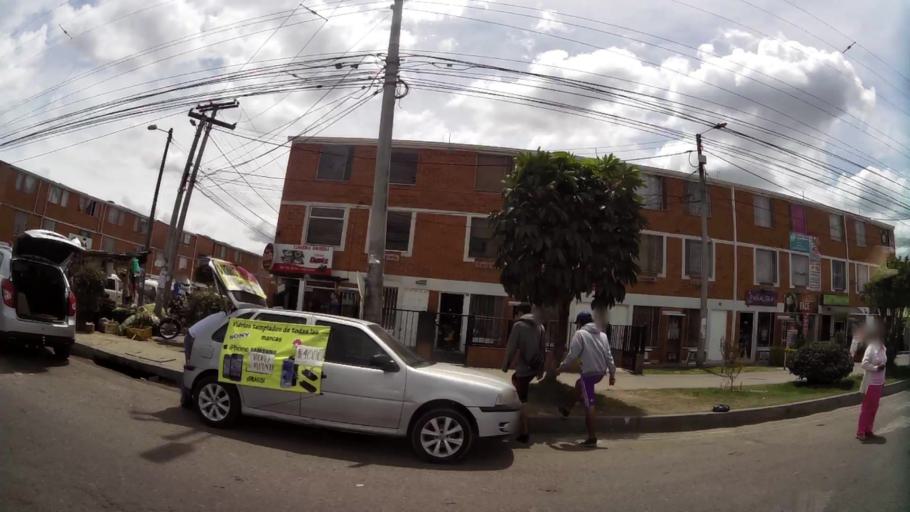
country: CO
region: Cundinamarca
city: Funza
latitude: 4.6519
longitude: -74.1588
